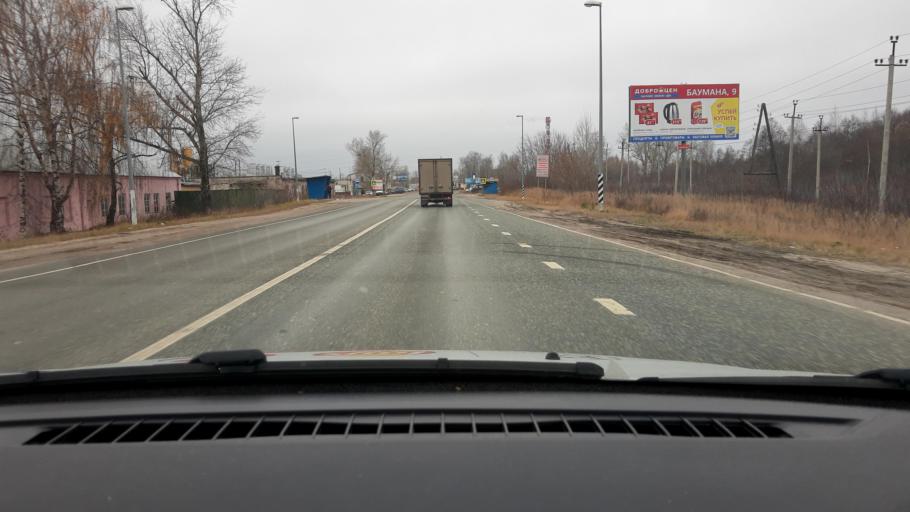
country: RU
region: Nizjnij Novgorod
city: Zavolzh'ye
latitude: 56.6227
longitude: 43.4267
